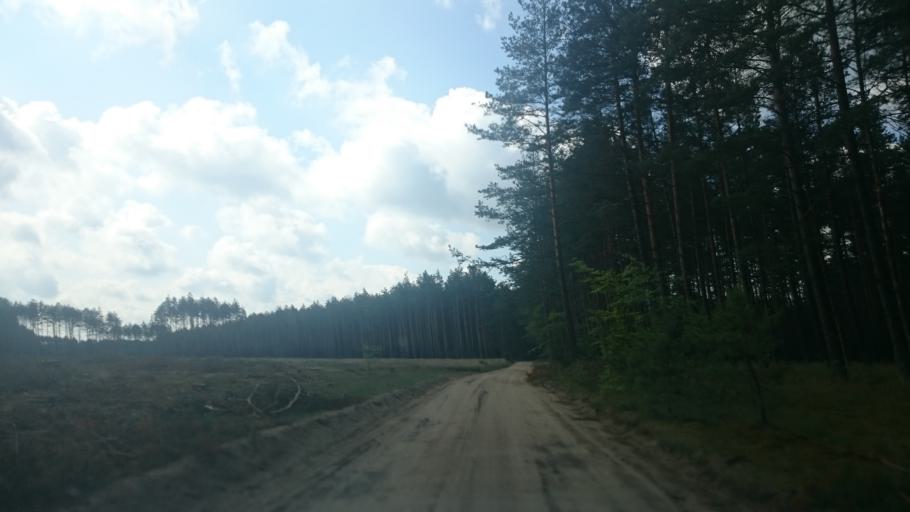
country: PL
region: Pomeranian Voivodeship
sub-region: Powiat koscierski
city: Karsin
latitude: 53.9920
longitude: 17.9340
